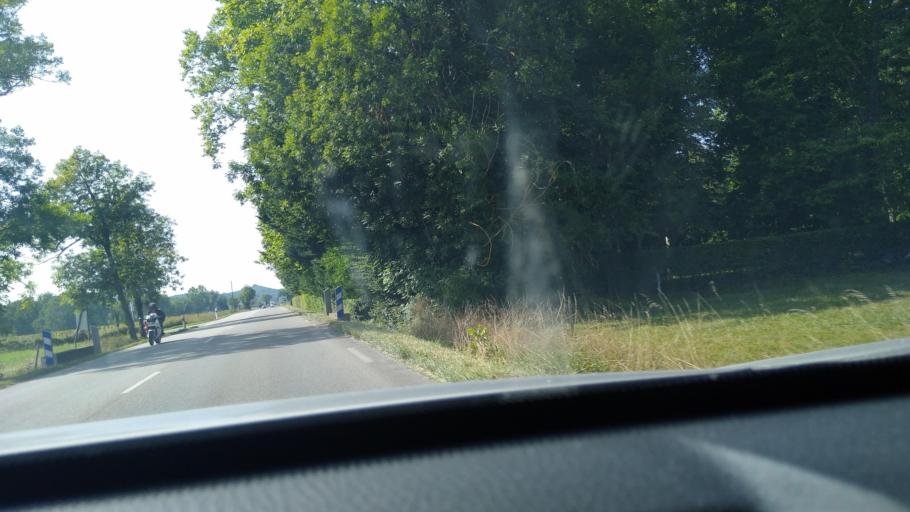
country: FR
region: Midi-Pyrenees
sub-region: Departement de l'Ariege
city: Saint-Lizier
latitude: 43.0176
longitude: 1.1049
